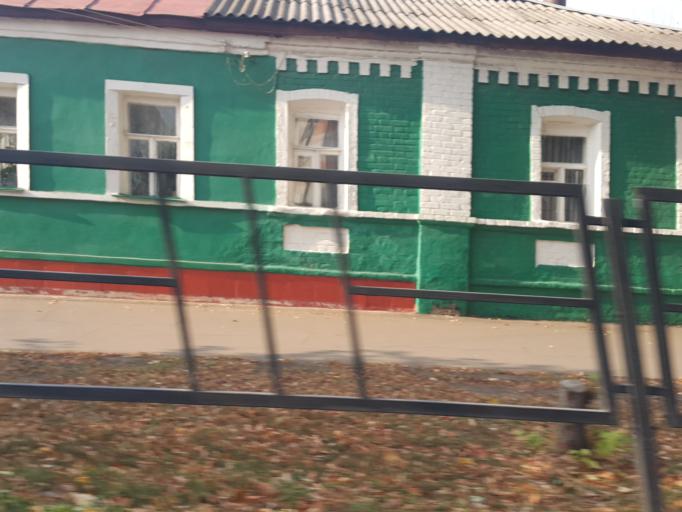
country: RU
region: Tambov
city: Tambov
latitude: 52.7044
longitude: 41.4657
